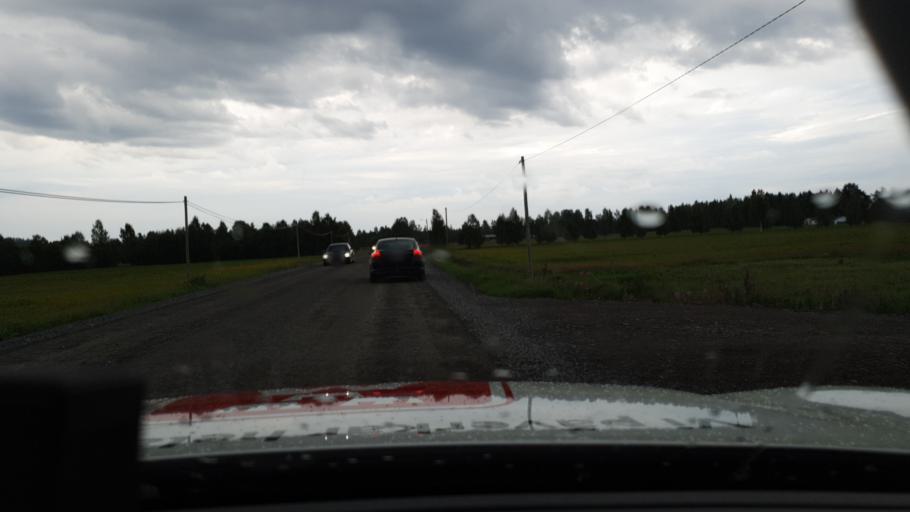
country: SE
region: Norrbotten
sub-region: Bodens Kommun
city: Boden
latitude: 65.8554
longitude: 21.4786
